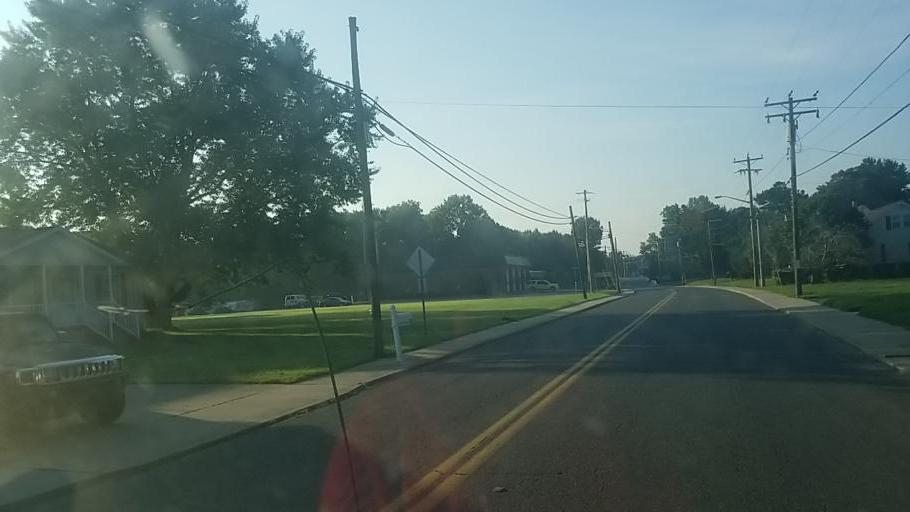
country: US
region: Delaware
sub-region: Sussex County
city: Selbyville
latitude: 38.4642
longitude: -75.2241
